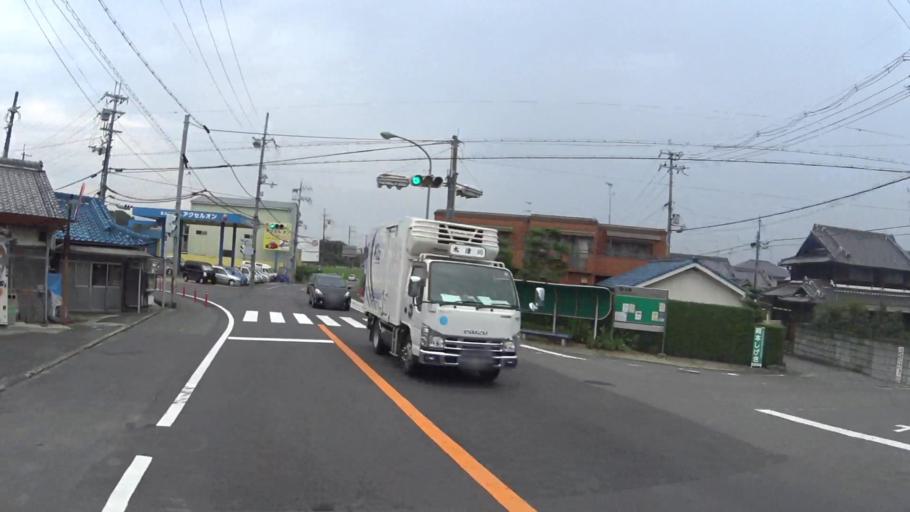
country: JP
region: Kyoto
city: Tanabe
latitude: 34.8329
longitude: 135.7549
